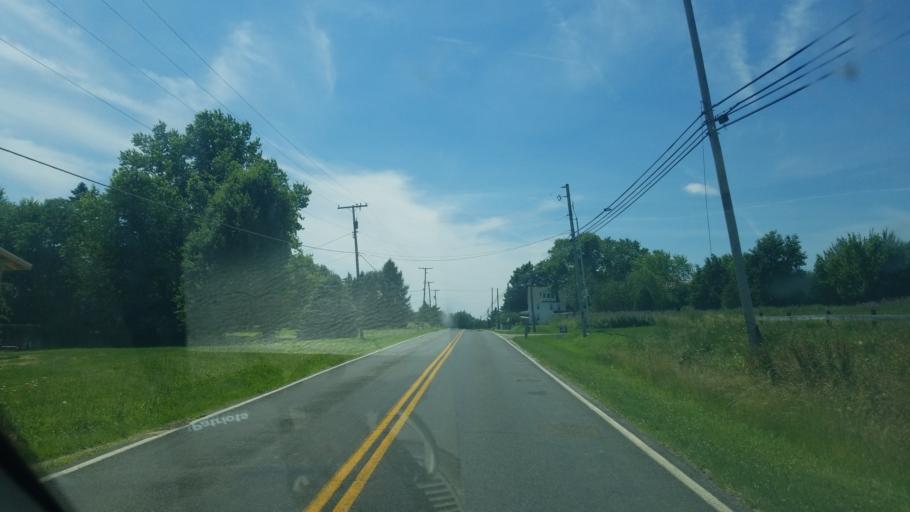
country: US
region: Ohio
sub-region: Stark County
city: Louisville
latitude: 40.8510
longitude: -81.2294
